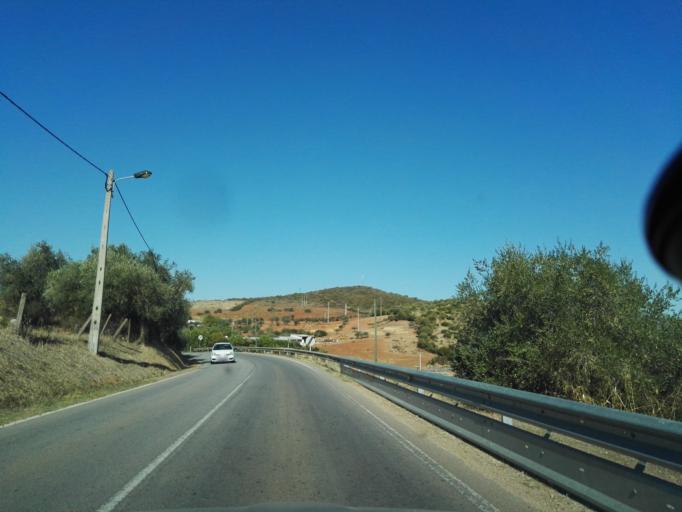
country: PT
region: Portalegre
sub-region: Elvas
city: Elvas
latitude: 38.8932
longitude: -7.1712
